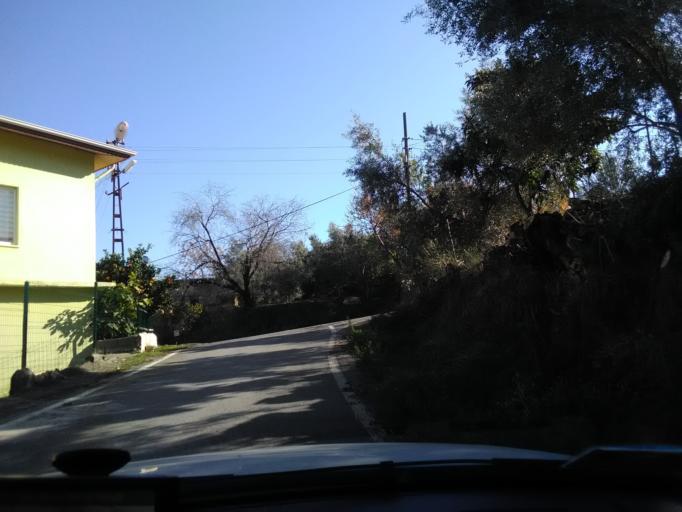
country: TR
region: Antalya
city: Gazipasa
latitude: 36.2473
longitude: 32.3369
